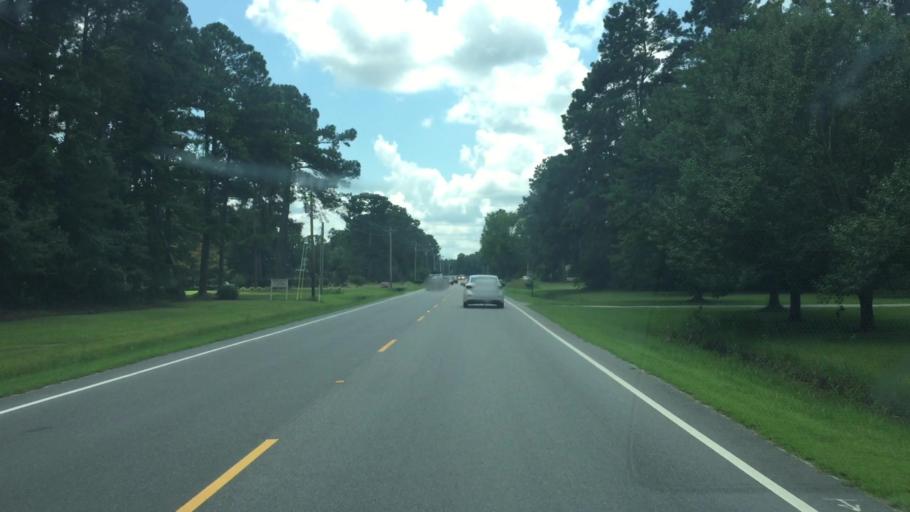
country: US
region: North Carolina
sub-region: Columbus County
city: Chadbourn
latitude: 34.2406
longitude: -78.8220
